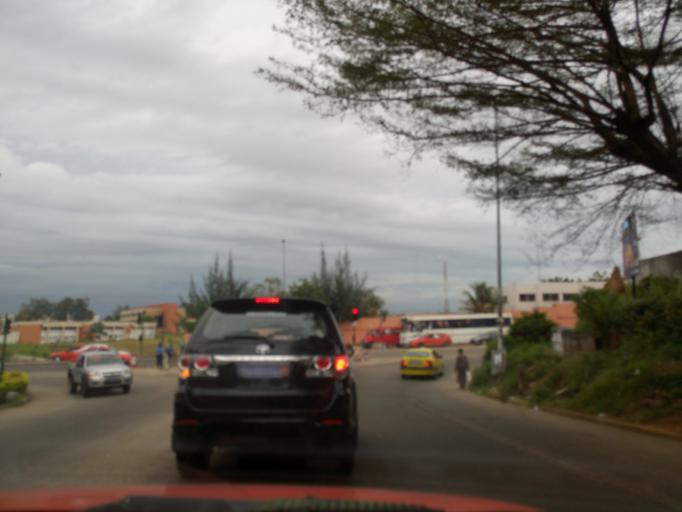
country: CI
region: Lagunes
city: Abidjan
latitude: 5.3499
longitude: -3.9912
